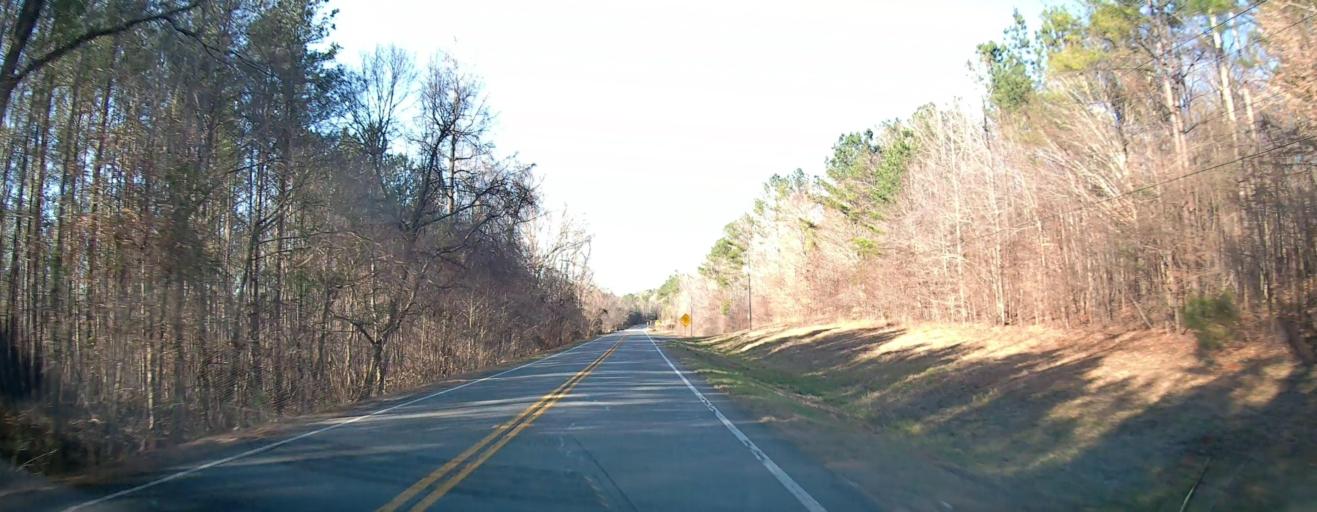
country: US
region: Georgia
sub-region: Talbot County
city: Talbotton
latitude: 32.7401
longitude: -84.5550
